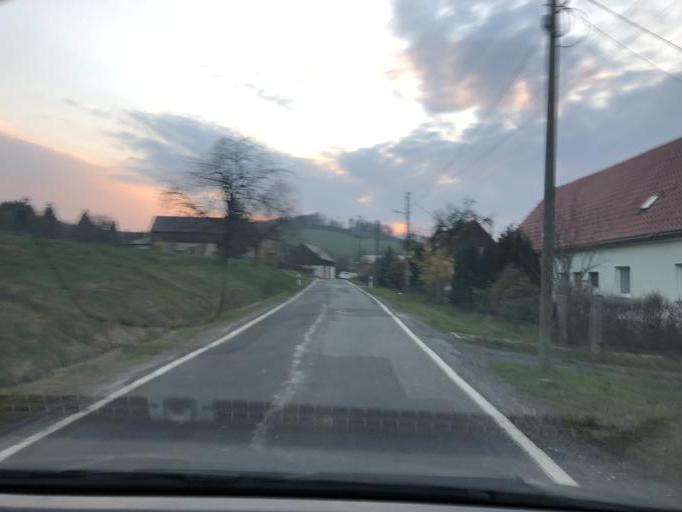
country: DE
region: Saxony
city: Kamenz
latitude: 51.2394
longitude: 14.0862
